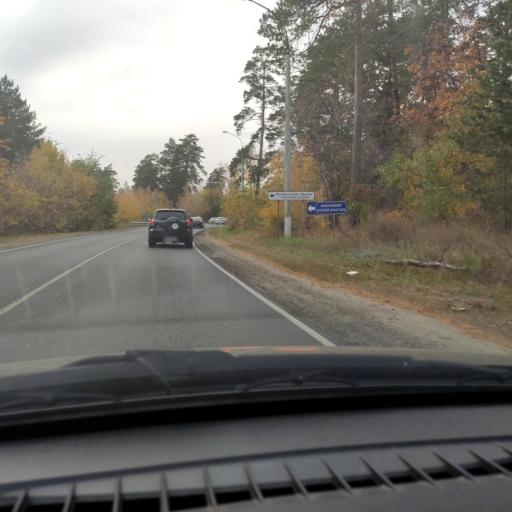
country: RU
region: Samara
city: Tol'yatti
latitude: 53.4735
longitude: 49.3812
